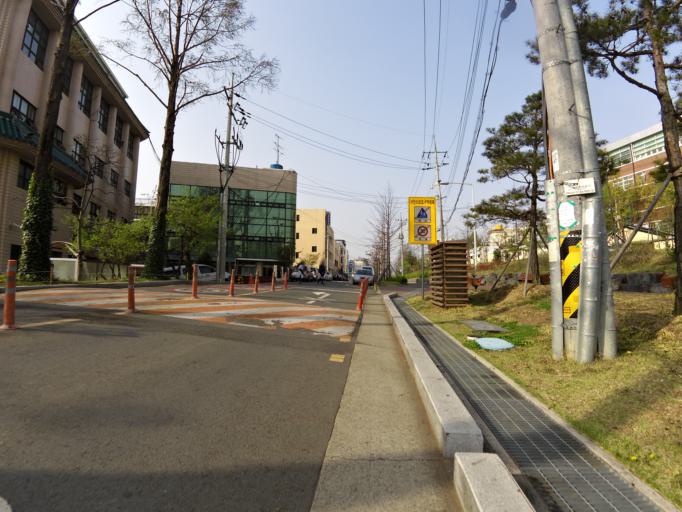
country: KR
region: Daegu
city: Daegu
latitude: 35.8865
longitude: 128.6362
